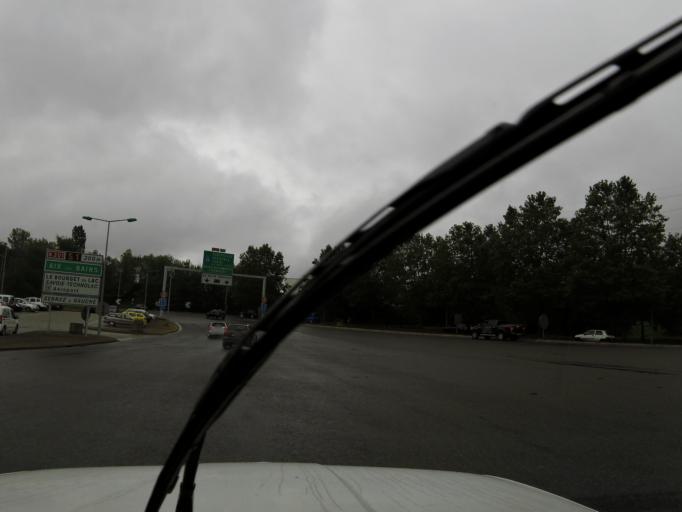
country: FR
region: Rhone-Alpes
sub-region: Departement de la Savoie
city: La Motte-Servolex
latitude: 45.6033
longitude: 5.8875
